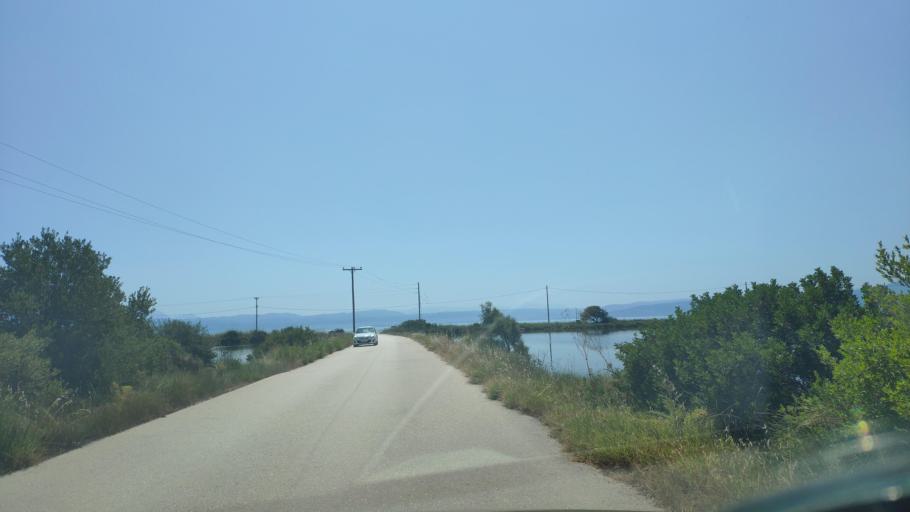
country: GR
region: Epirus
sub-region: Nomos Artas
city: Aneza
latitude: 39.0123
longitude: 20.9238
